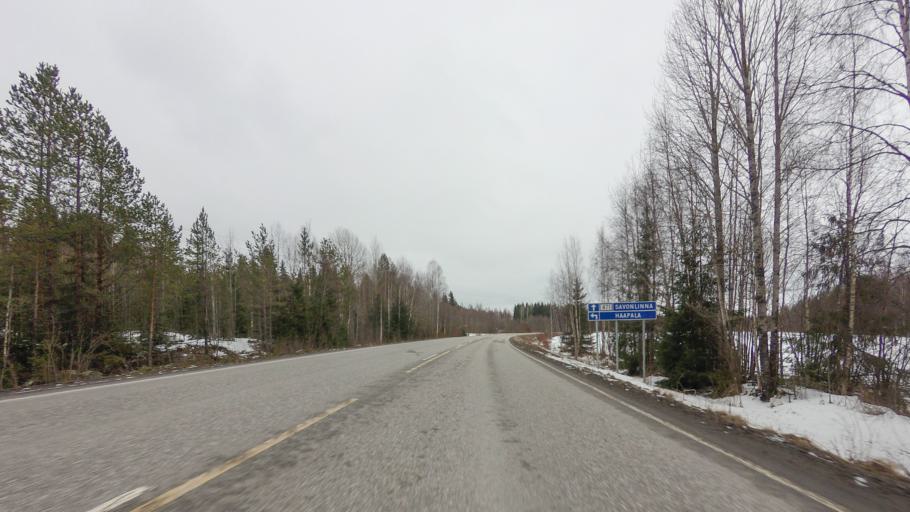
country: FI
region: Southern Savonia
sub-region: Savonlinna
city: Savonlinna
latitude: 61.9089
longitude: 28.9270
